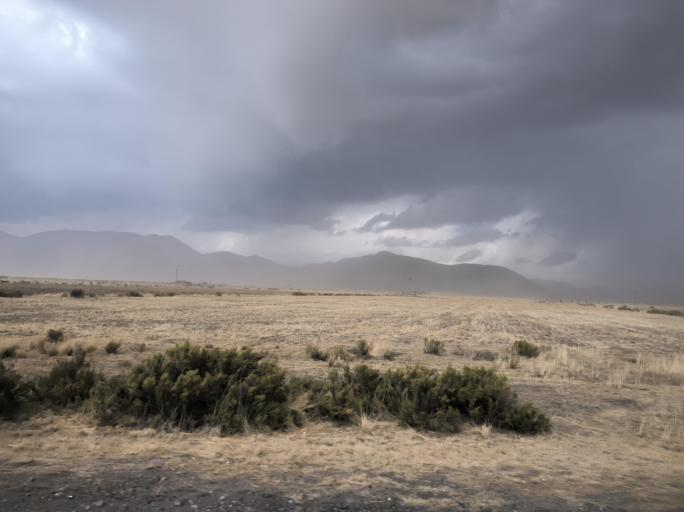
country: BO
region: Oruro
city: Challapata
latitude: -18.7859
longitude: -66.8479
